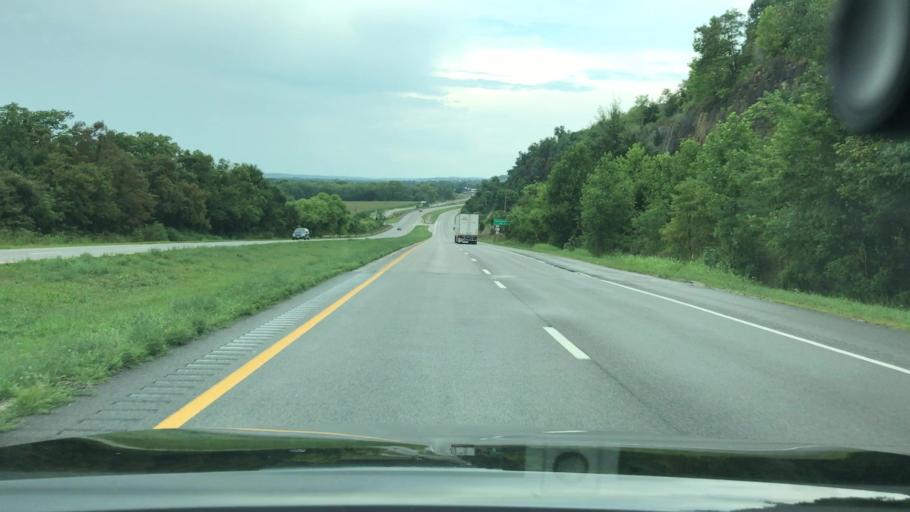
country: US
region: West Virginia
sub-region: Mason County
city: Point Pleasant
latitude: 38.8206
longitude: -82.1218
